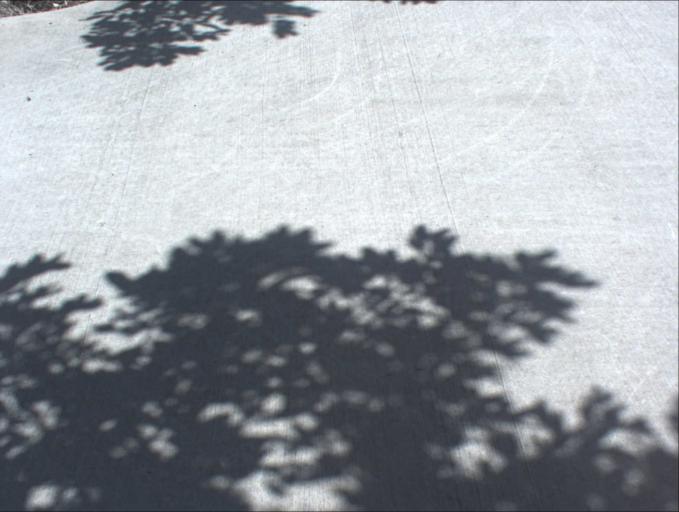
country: AU
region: Queensland
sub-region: Logan
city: Chambers Flat
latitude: -27.8011
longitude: 153.1086
